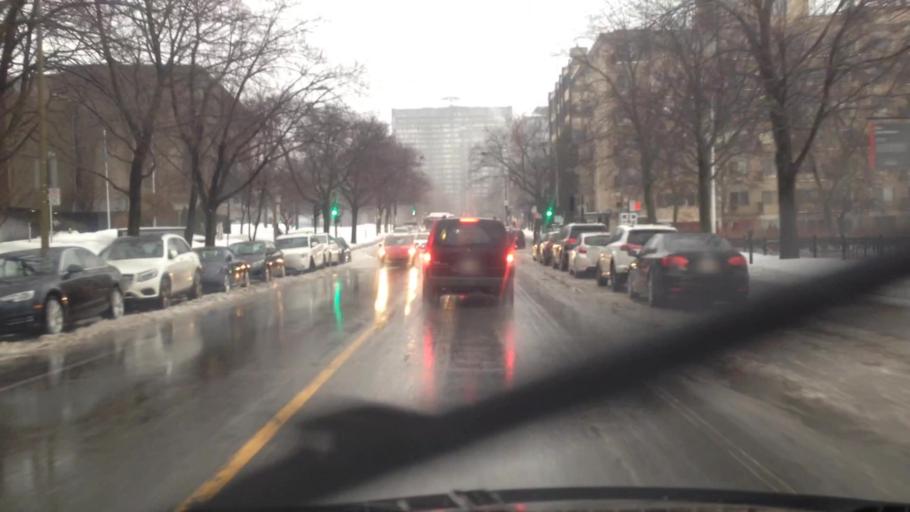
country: CA
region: Quebec
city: Westmount
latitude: 45.4975
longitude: -73.6193
